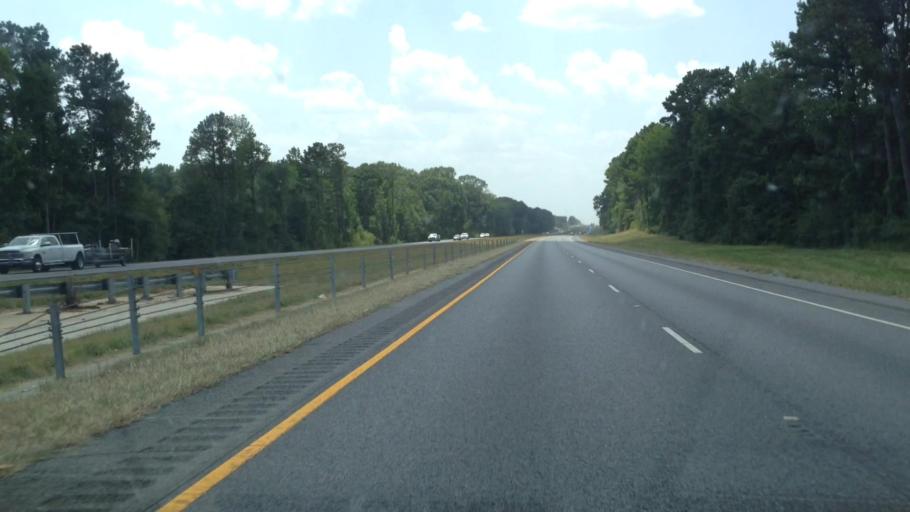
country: US
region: Louisiana
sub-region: Lincoln Parish
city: Ruston
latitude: 32.5296
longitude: -92.4541
